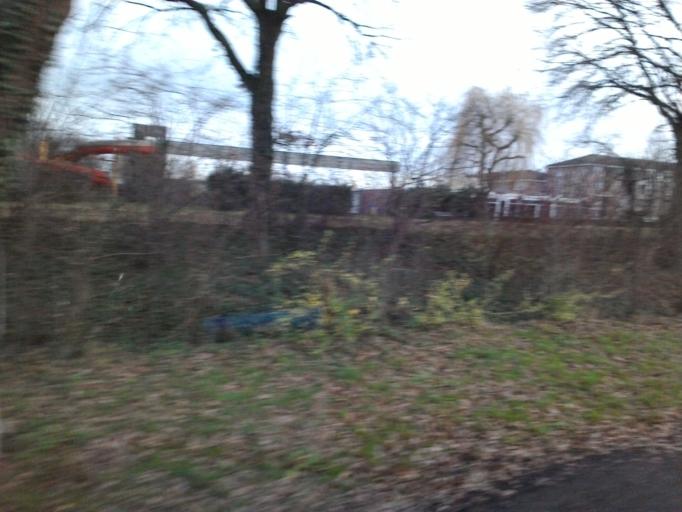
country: NL
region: North Brabant
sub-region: Gemeente Sint-Oedenrode
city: Sint-Oedenrode
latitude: 51.5669
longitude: 5.4580
